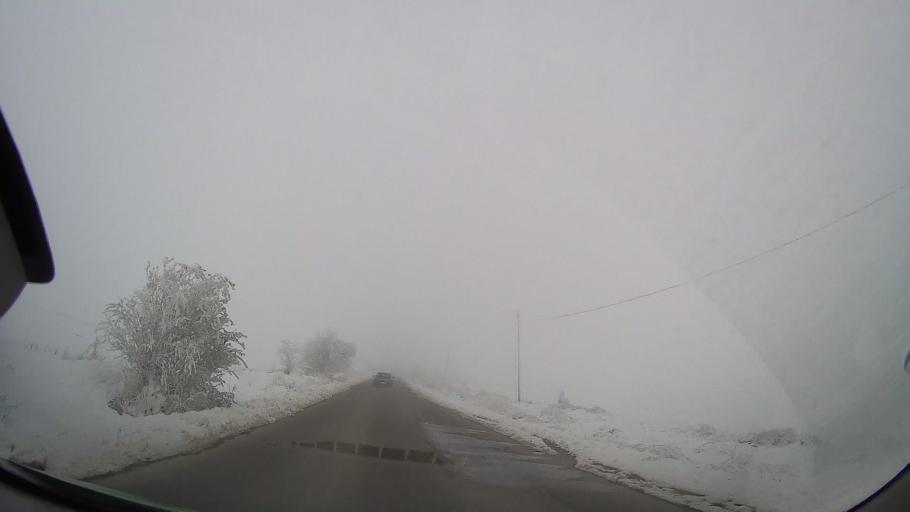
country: RO
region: Neamt
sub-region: Comuna Sabaoani
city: Sabaoani
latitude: 46.9944
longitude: 26.8630
